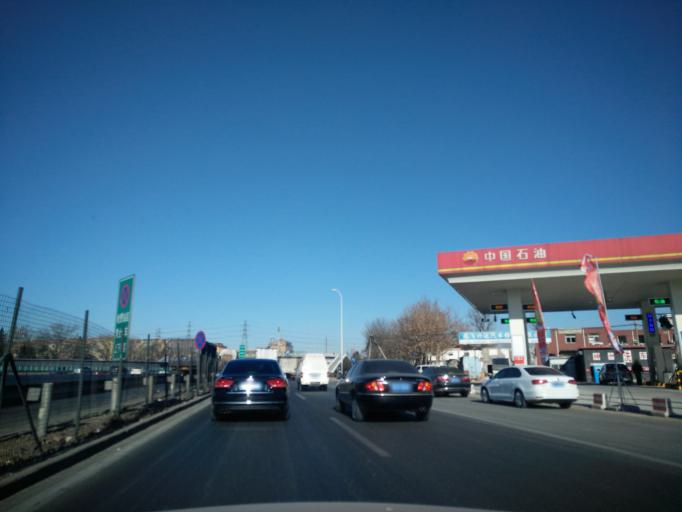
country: CN
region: Beijing
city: Xihongmen
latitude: 39.7976
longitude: 116.3416
